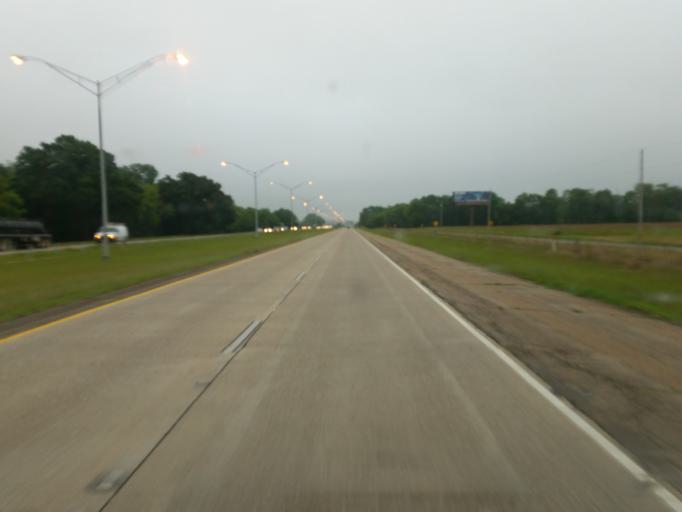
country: US
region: Louisiana
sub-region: Bossier Parish
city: Red Chute
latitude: 32.5344
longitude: -93.6506
